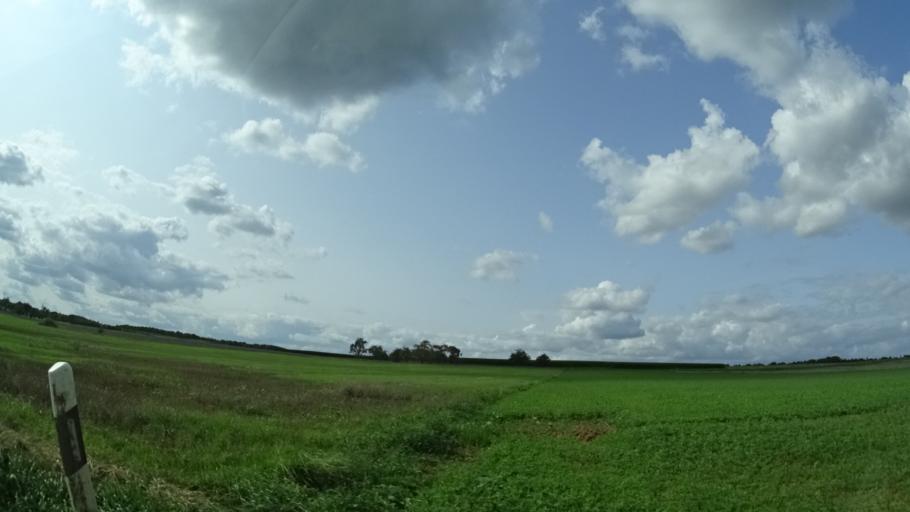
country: DE
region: Bavaria
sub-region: Regierungsbezirk Unterfranken
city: Arnstein
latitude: 49.9327
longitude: 9.9749
